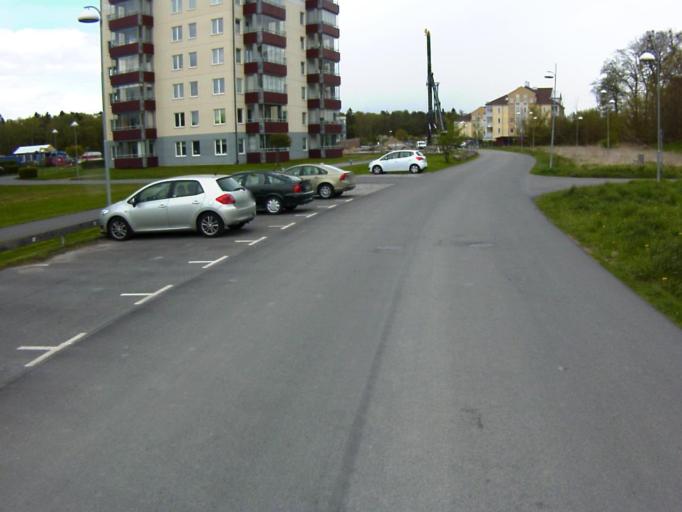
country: SE
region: Skane
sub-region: Kristianstads Kommun
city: Kristianstad
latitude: 56.0436
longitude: 14.1665
